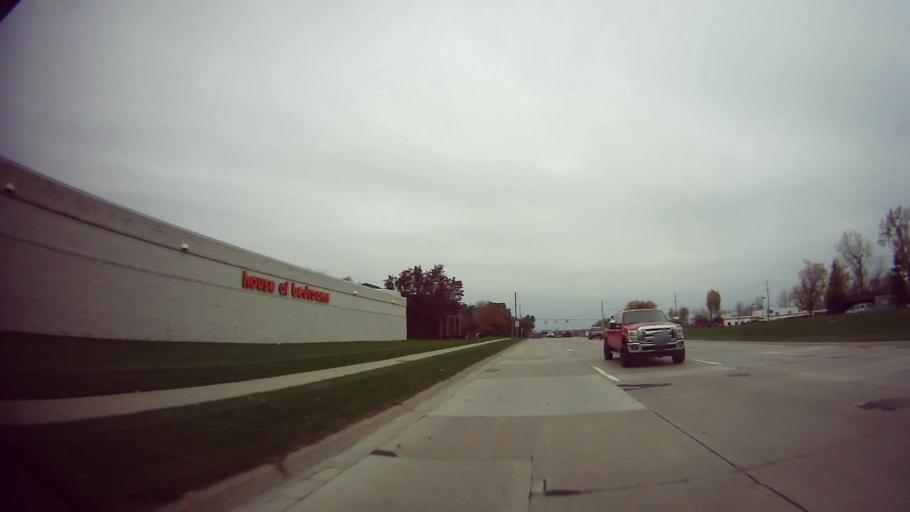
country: US
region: Michigan
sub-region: Oakland County
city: Sylvan Lake
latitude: 42.6152
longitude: -83.3124
